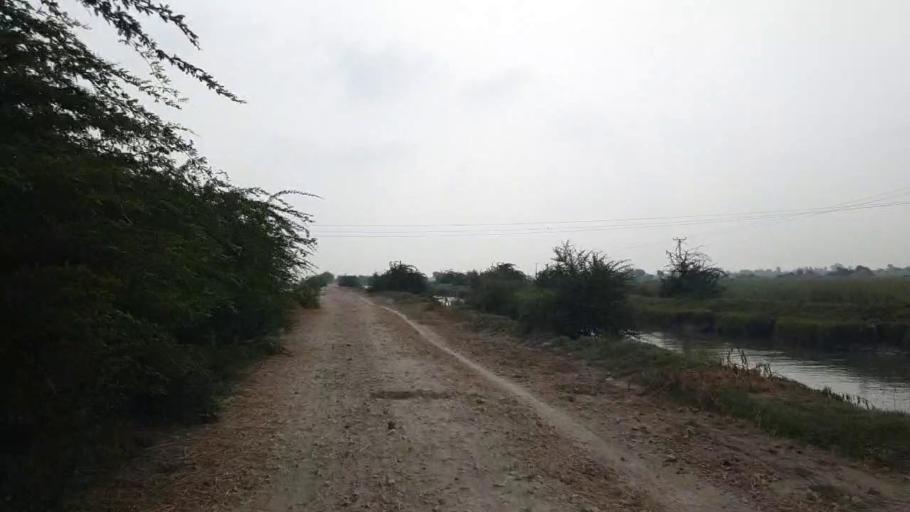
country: PK
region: Sindh
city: Kario
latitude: 24.8617
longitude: 68.5198
